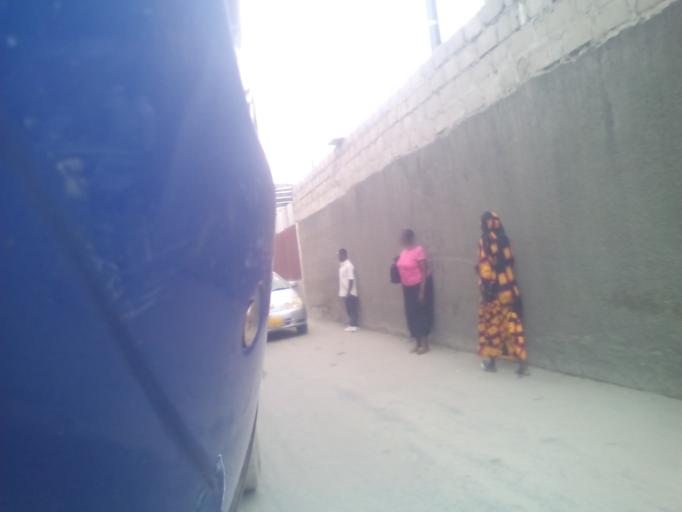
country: TZ
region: Dar es Salaam
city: Dar es Salaam
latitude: -6.8524
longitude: 39.2302
